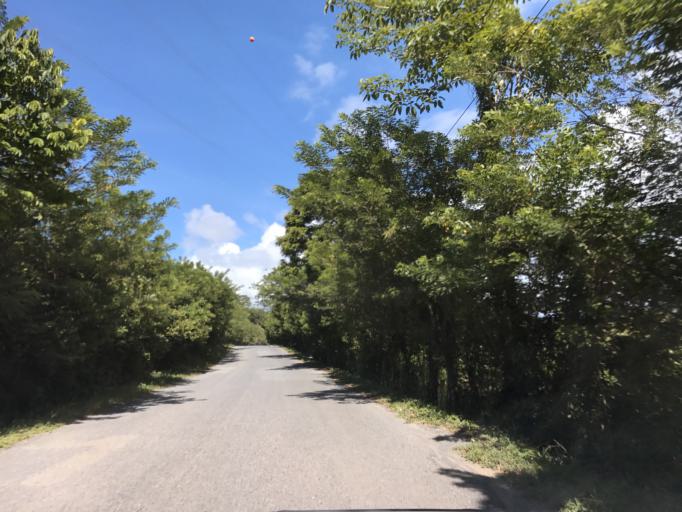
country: GT
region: Izabal
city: Morales
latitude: 15.6465
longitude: -89.0172
